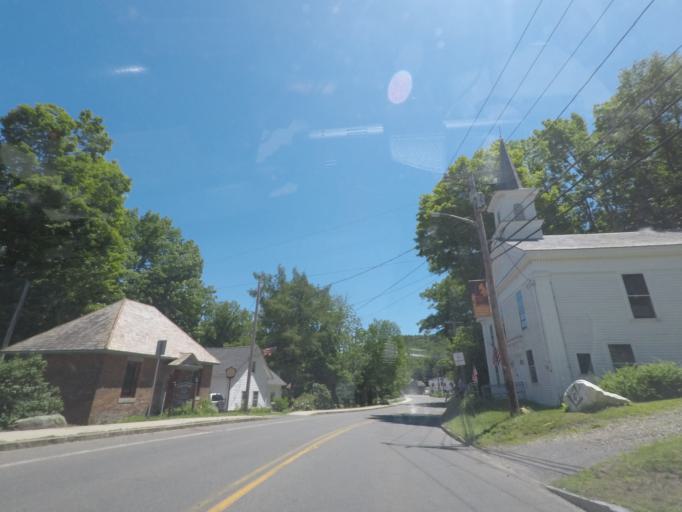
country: US
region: Massachusetts
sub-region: Berkshire County
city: Becket
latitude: 42.2789
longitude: -72.9813
